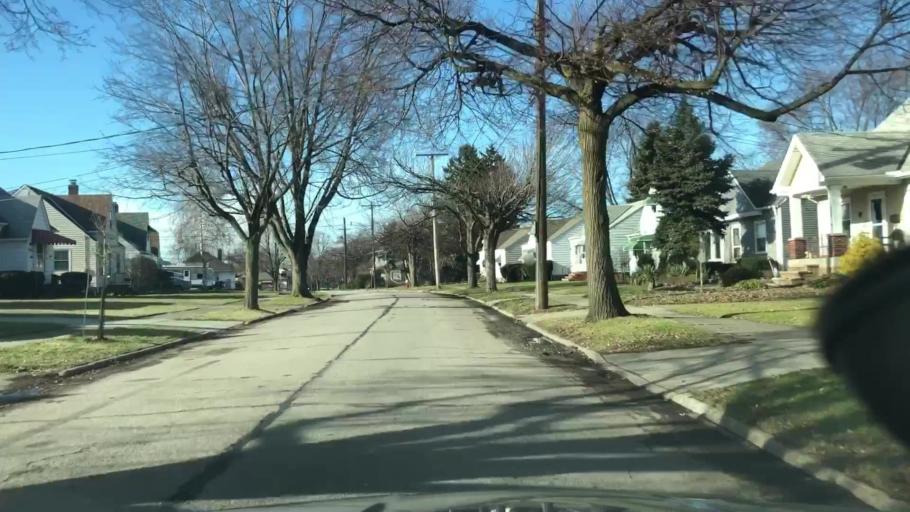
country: US
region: Ohio
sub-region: Cuyahoga County
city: Brooklyn
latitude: 41.4279
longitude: -81.7329
